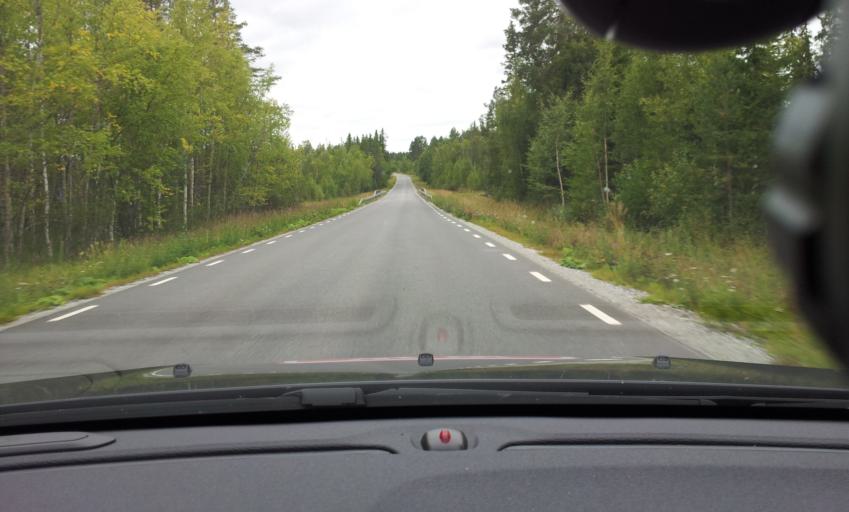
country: SE
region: Jaemtland
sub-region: Braecke Kommun
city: Braecke
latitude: 63.0858
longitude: 15.4258
